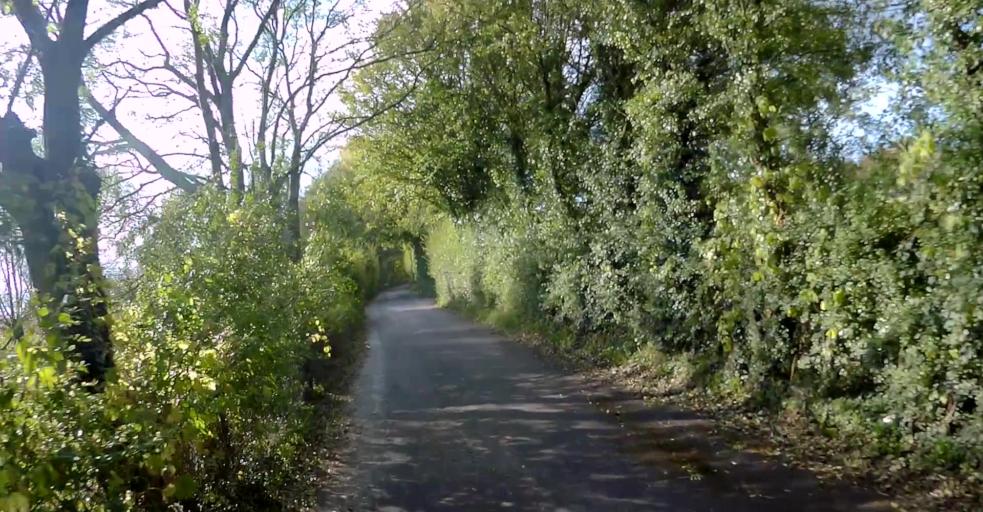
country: GB
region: England
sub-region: Surrey
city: Farnham
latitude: 51.2022
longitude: -0.8216
